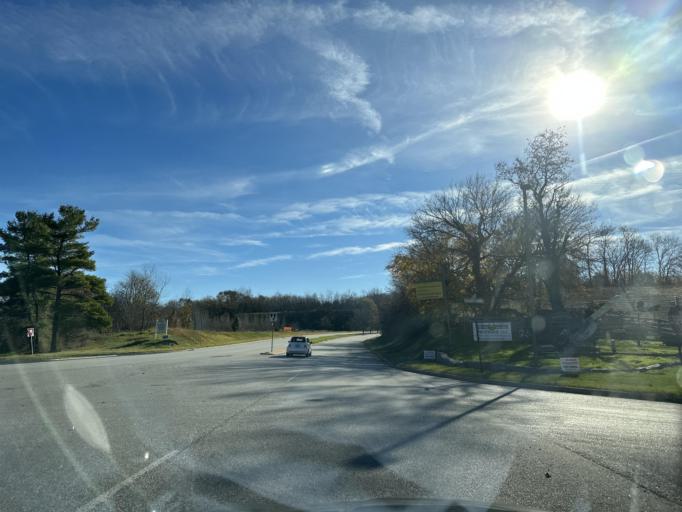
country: US
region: Virginia
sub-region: City of Staunton
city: Staunton
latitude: 38.1527
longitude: -79.0552
